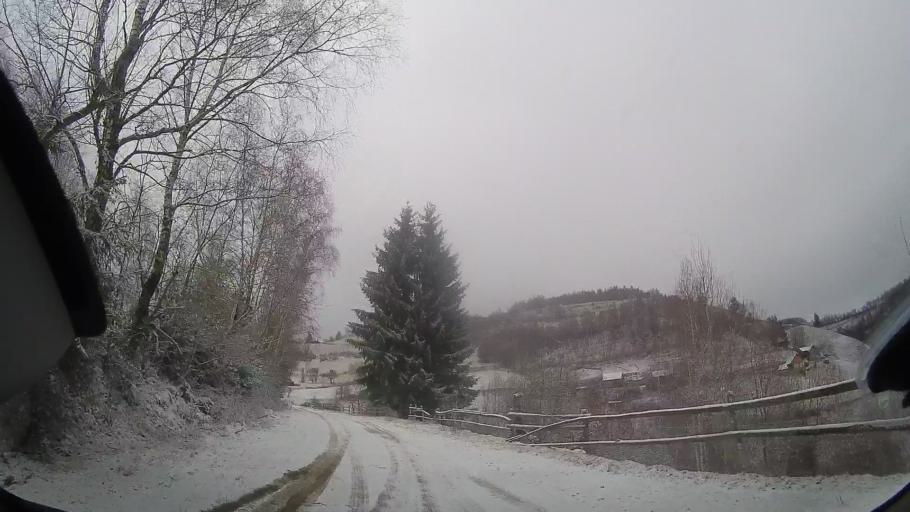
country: RO
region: Cluj
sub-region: Comuna Maguri-Racatau
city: Maguri-Racatau
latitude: 46.6638
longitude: 23.1902
